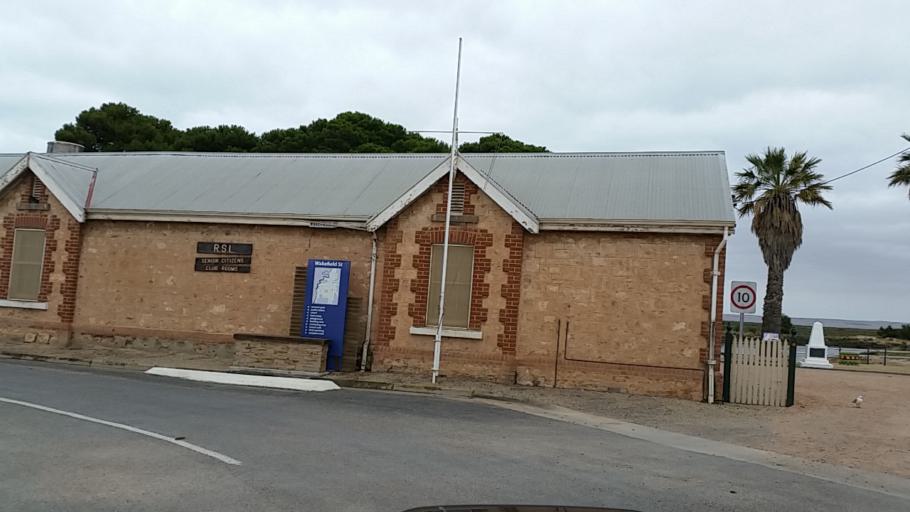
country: AU
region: South Australia
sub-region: Wakefield
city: Balaklava
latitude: -34.1849
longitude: 138.1463
